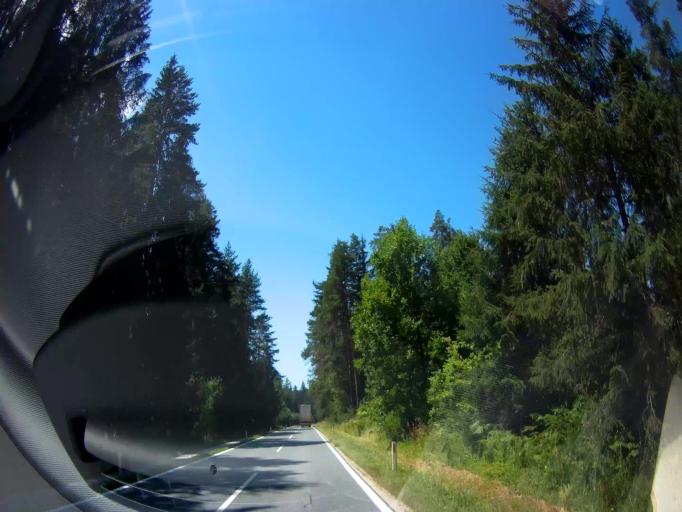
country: AT
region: Carinthia
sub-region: Politischer Bezirk Volkermarkt
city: Eberndorf
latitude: 46.6129
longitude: 14.6678
